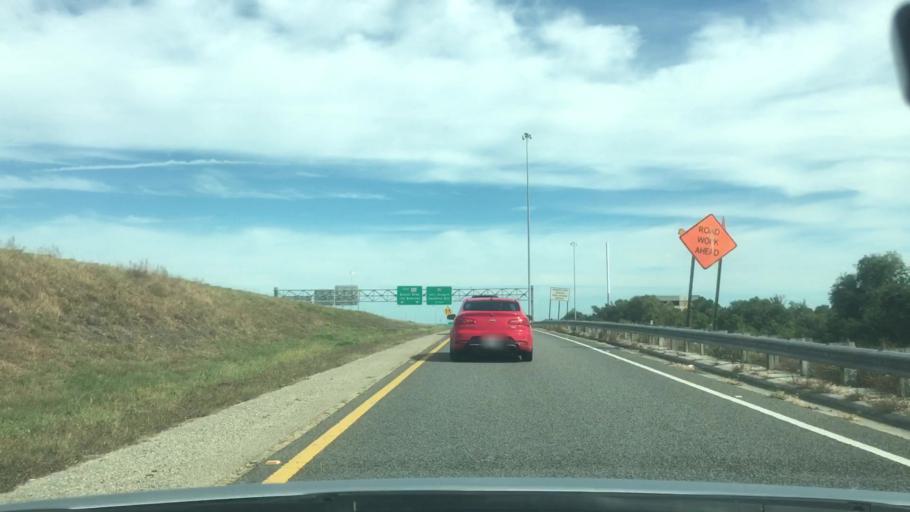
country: US
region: Florida
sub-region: Duval County
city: Jacksonville Beach
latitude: 30.2499
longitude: -81.5334
